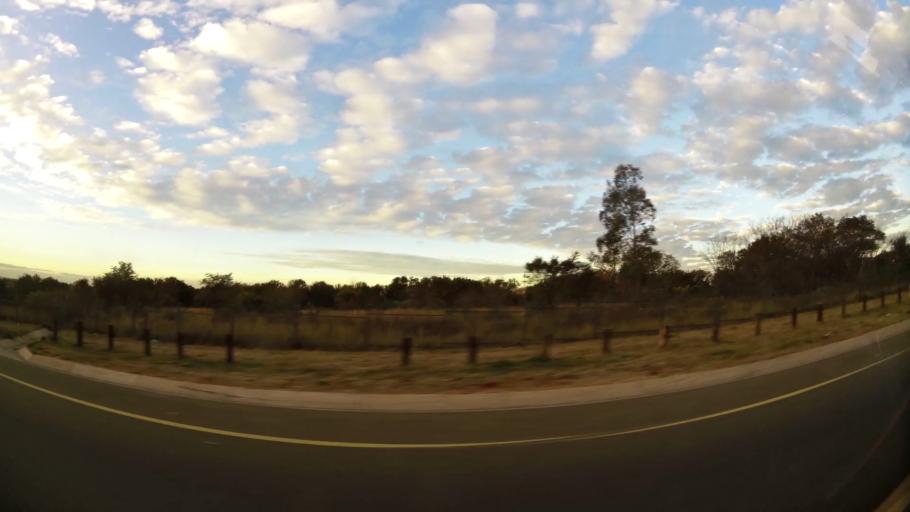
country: ZA
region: Gauteng
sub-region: City of Tshwane Metropolitan Municipality
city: Pretoria
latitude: -25.7465
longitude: 28.2693
